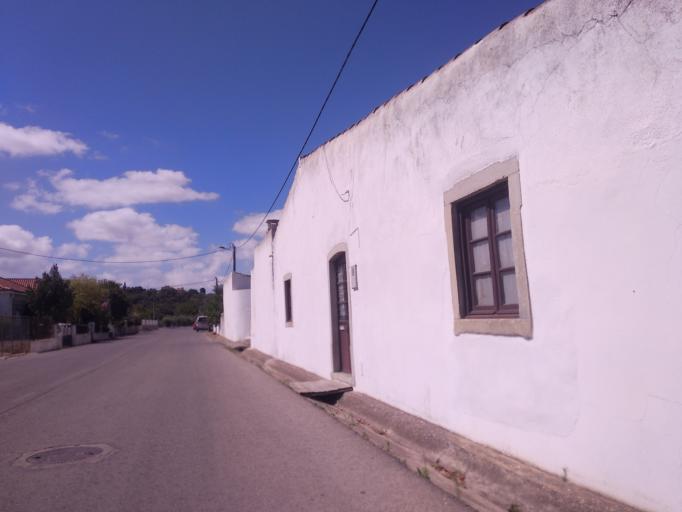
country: PT
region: Faro
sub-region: Sao Bras de Alportel
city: Sao Bras de Alportel
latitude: 37.1691
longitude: -7.8906
